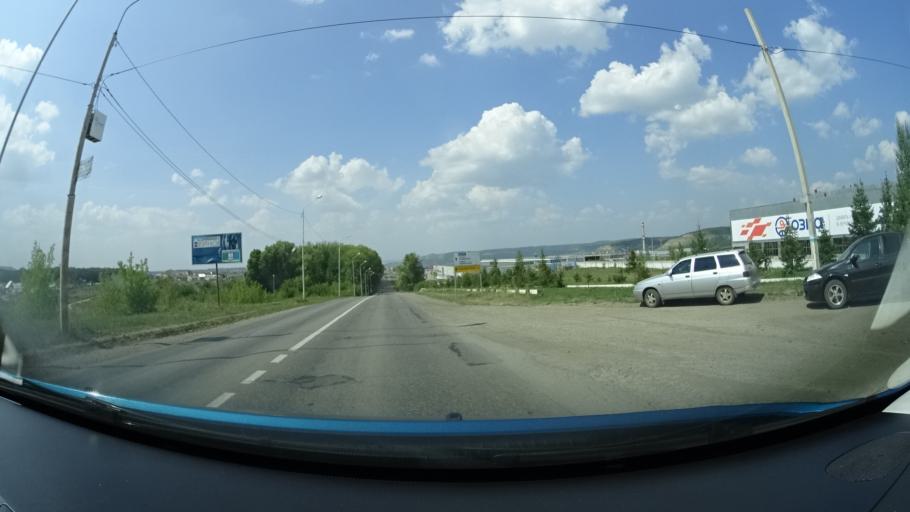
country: RU
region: Bashkortostan
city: Oktyabr'skiy
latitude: 54.4798
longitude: 53.5586
